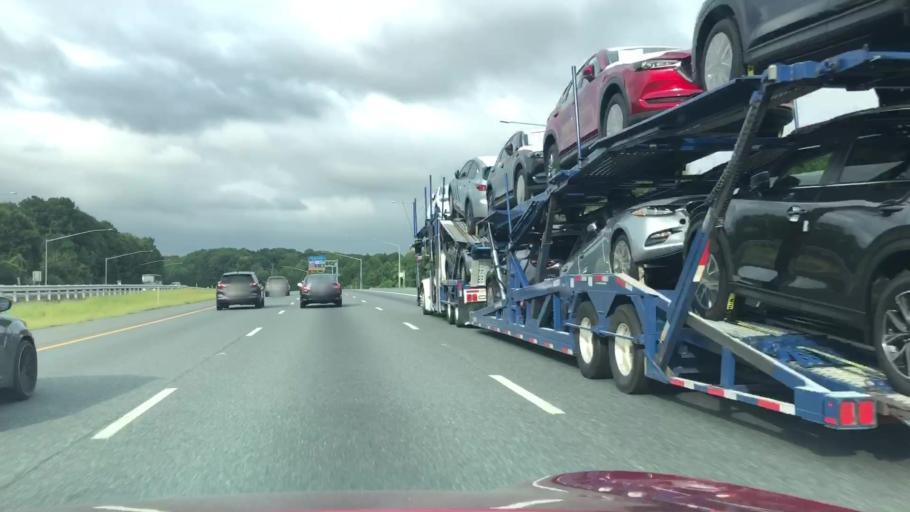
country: US
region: Maryland
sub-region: Harford County
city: Riverside
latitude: 39.4884
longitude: -76.2480
